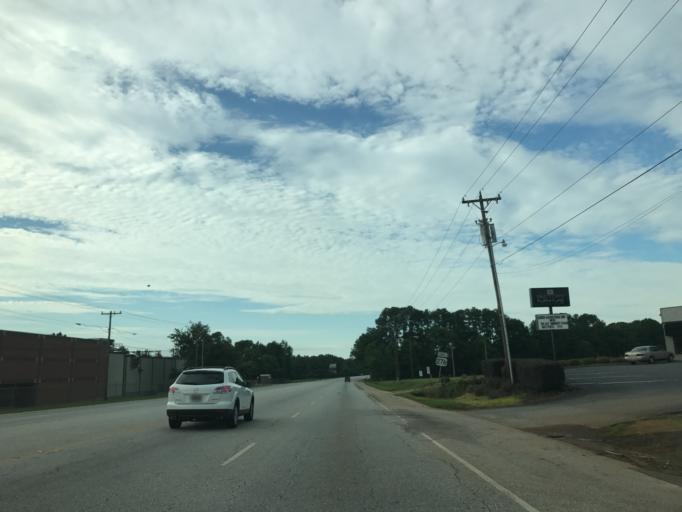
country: US
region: South Carolina
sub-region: Greenville County
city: Mauldin
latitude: 34.7975
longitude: -82.3155
